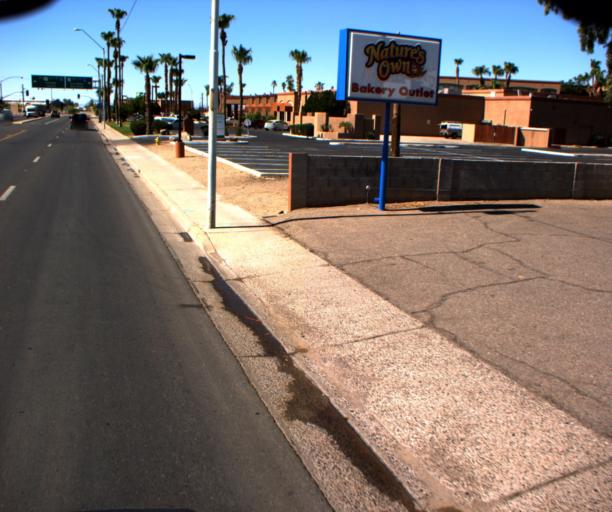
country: US
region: Arizona
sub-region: Pinal County
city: Casa Grande
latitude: 32.8813
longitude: -111.7574
